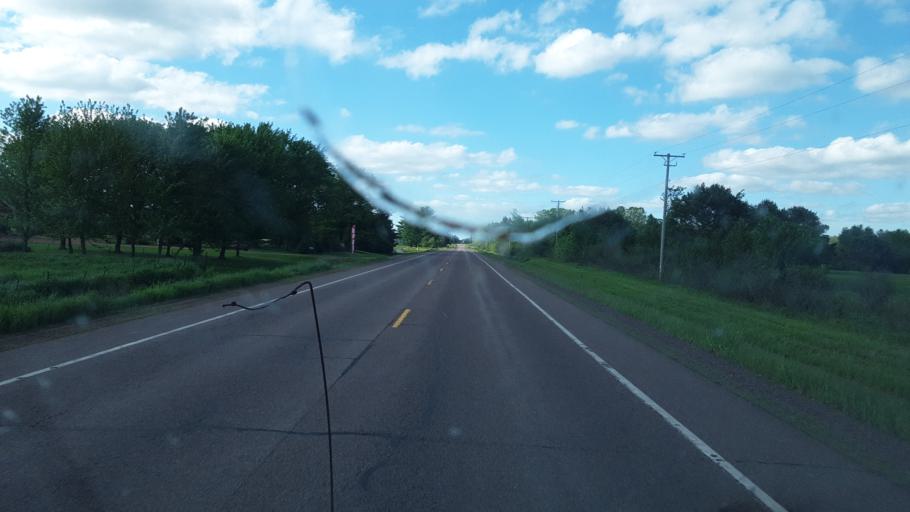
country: US
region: Wisconsin
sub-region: Wood County
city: Marshfield
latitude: 44.4897
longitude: -90.1804
